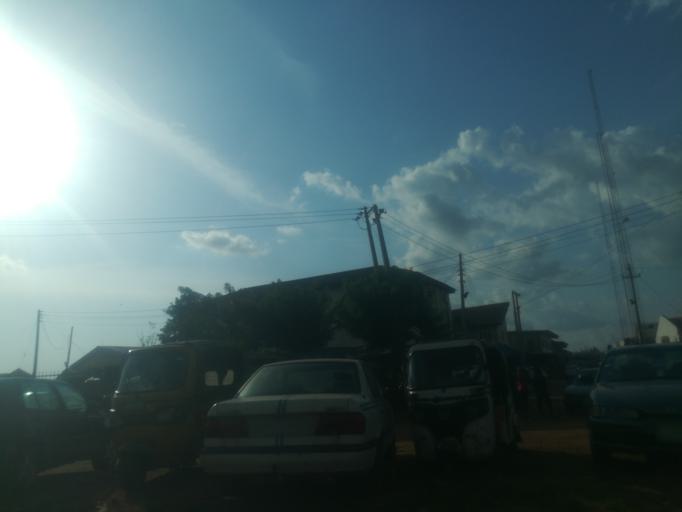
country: NG
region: Oyo
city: Ibadan
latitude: 7.3891
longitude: 3.8187
